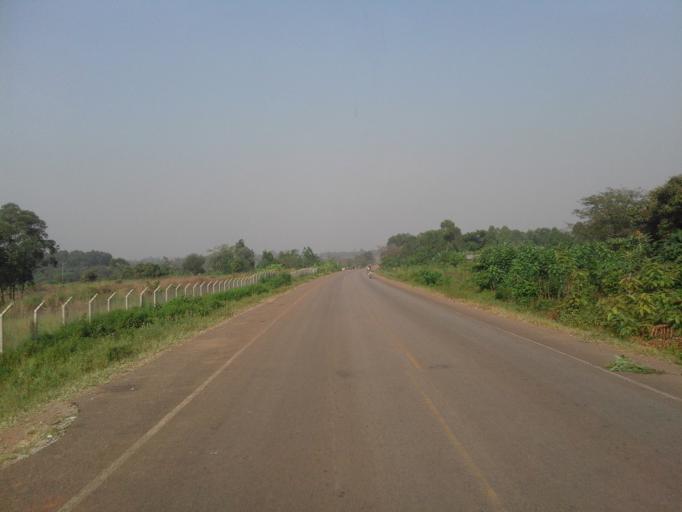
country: UG
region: Eastern Region
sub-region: Mbale District
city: Mbale
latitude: 1.0740
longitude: 34.1164
